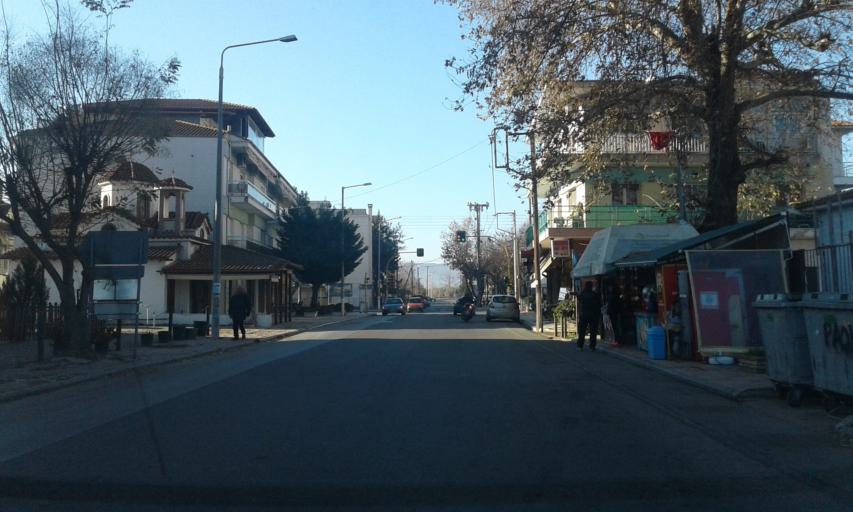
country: GR
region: Central Macedonia
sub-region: Nomos Thessalonikis
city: Lagkadas
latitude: 40.7475
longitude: 23.0721
